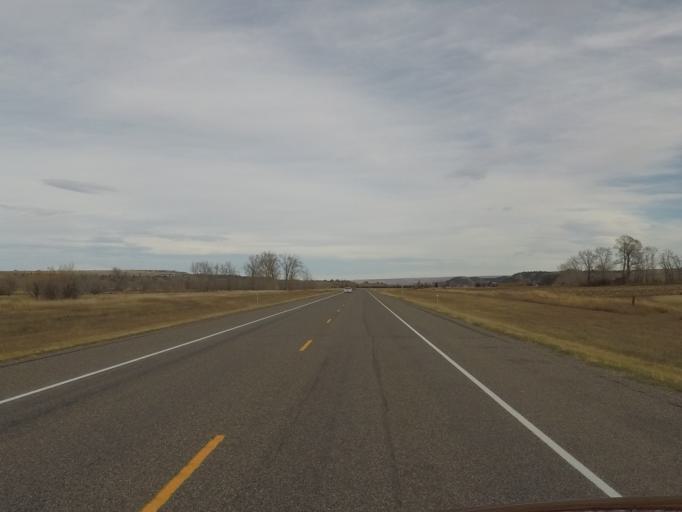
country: US
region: Montana
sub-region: Stillwater County
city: Columbus
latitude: 45.4652
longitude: -109.0437
